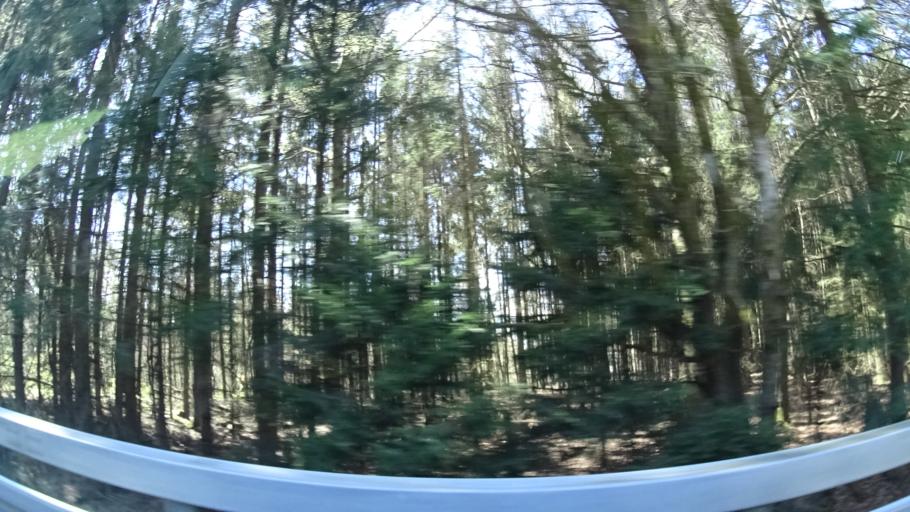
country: DE
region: Bavaria
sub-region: Upper Palatinate
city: Lauterhofen
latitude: 49.4129
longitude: 11.5993
